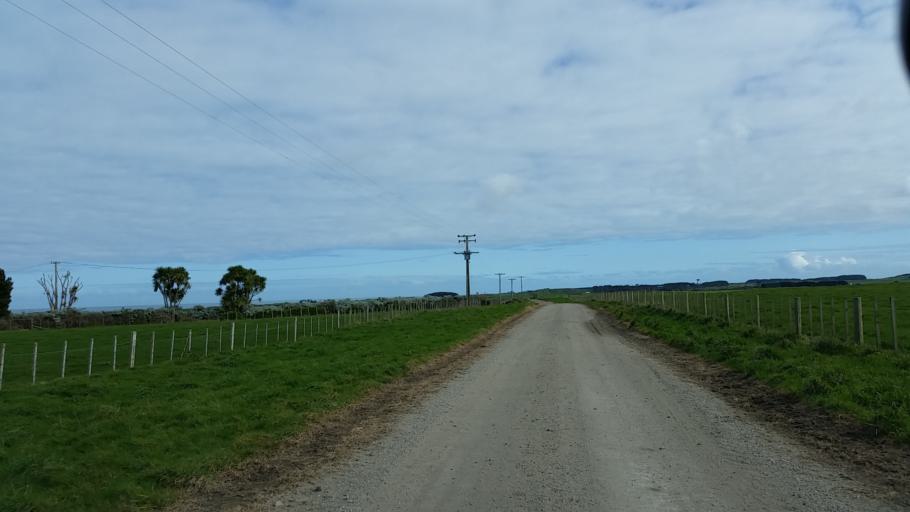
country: NZ
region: Taranaki
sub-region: South Taranaki District
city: Patea
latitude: -39.8070
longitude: 174.6520
